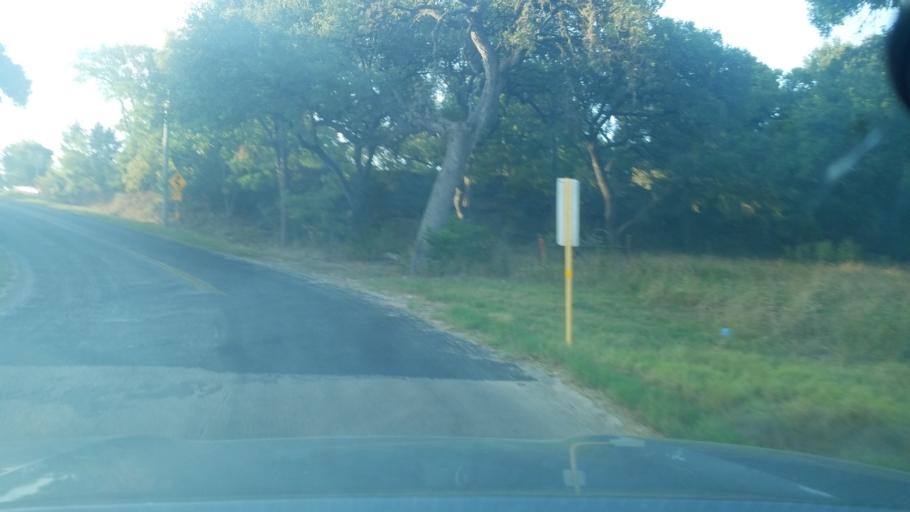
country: US
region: Texas
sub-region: Comal County
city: Bulverde
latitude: 29.7330
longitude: -98.4523
